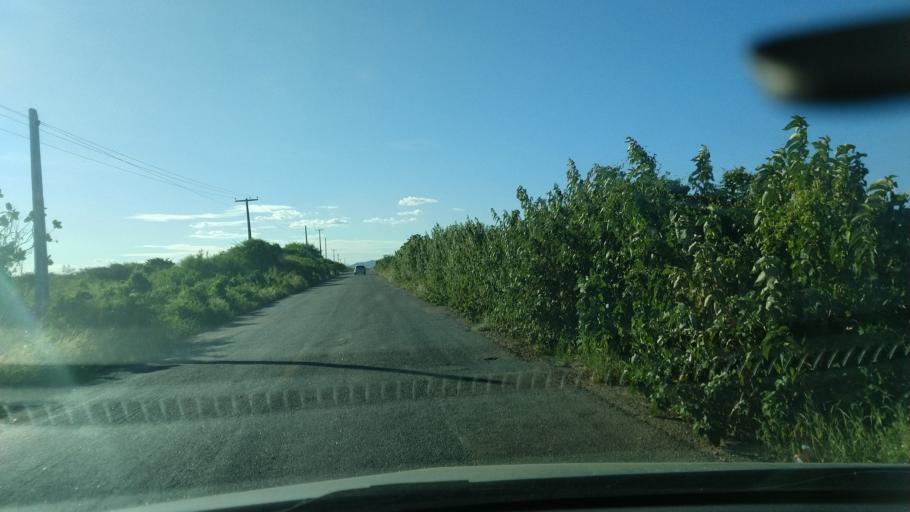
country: BR
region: Rio Grande do Norte
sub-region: Sao Jose Do Campestre
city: Sao Jose do Campestre
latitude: -6.4021
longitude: -35.6550
